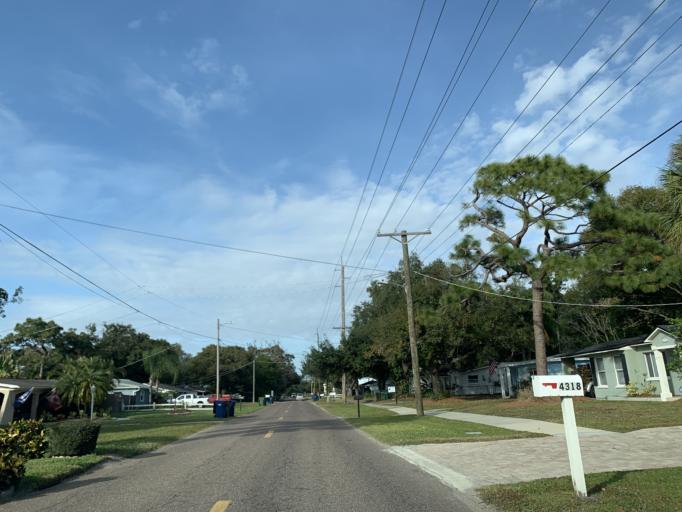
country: US
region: Florida
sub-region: Hillsborough County
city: Tampa
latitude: 27.9025
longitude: -82.5123
